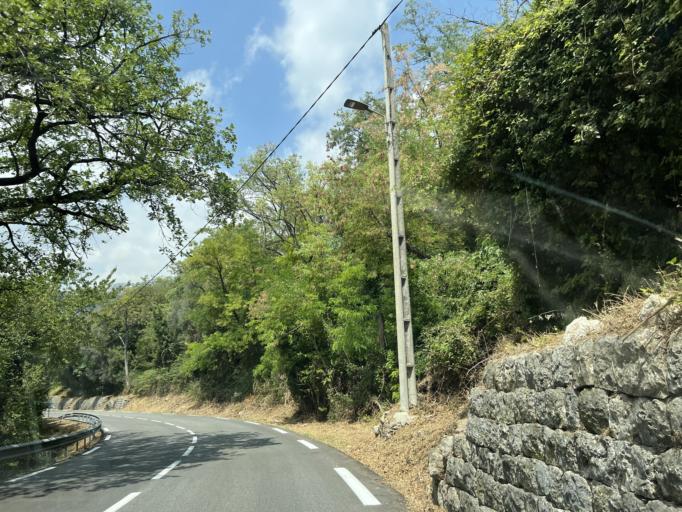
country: FR
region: Provence-Alpes-Cote d'Azur
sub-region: Departement des Alpes-Maritimes
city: Le Rouret
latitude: 43.7041
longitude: 7.0128
